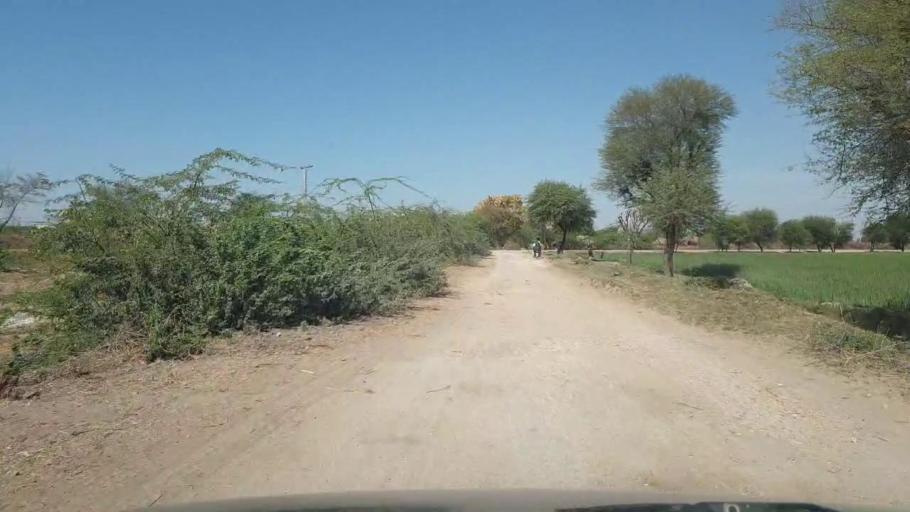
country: PK
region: Sindh
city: Dhoro Naro
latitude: 25.4692
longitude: 69.6066
